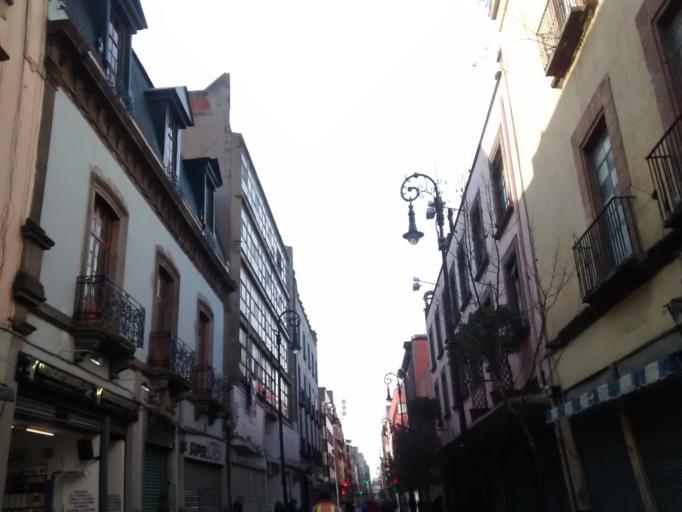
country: MX
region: Mexico City
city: Mexico City
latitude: 19.4304
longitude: -99.1304
